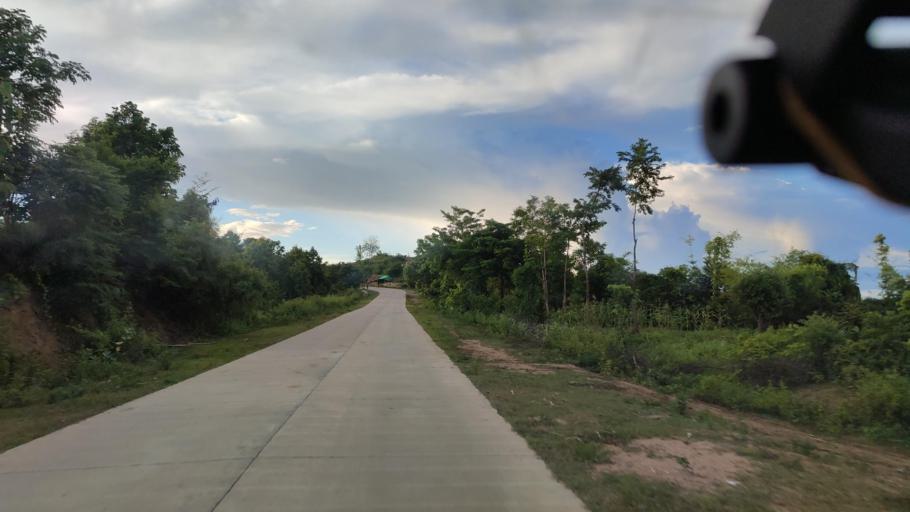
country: MM
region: Magway
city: Taungdwingyi
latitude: 20.0346
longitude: 95.7865
